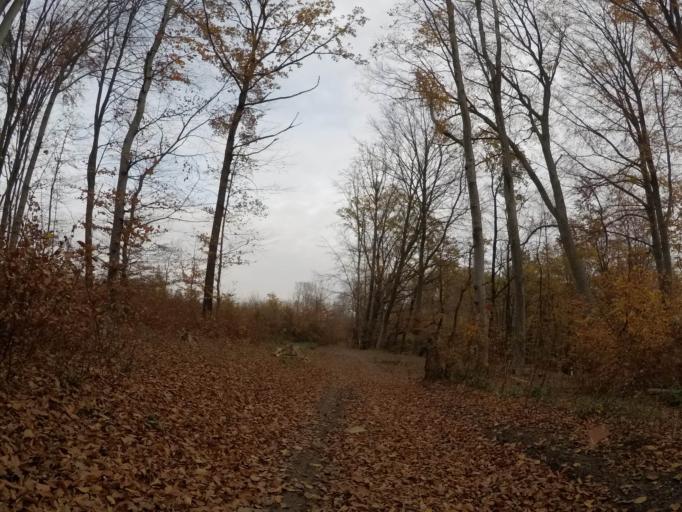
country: SK
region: Presovsky
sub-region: Okres Presov
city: Presov
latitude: 48.9405
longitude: 21.1301
